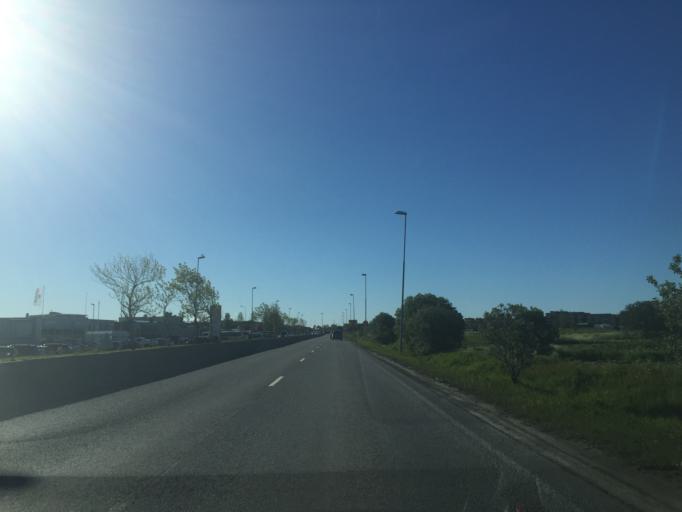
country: NO
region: Nordland
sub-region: Bodo
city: Bodo
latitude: 67.2794
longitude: 14.4282
